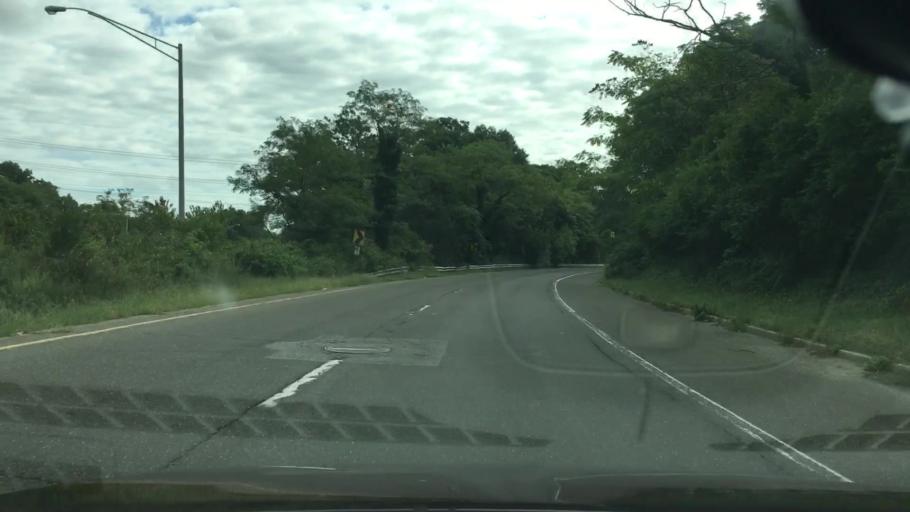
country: US
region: New York
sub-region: Suffolk County
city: Dix Hills
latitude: 40.8024
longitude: -73.3255
